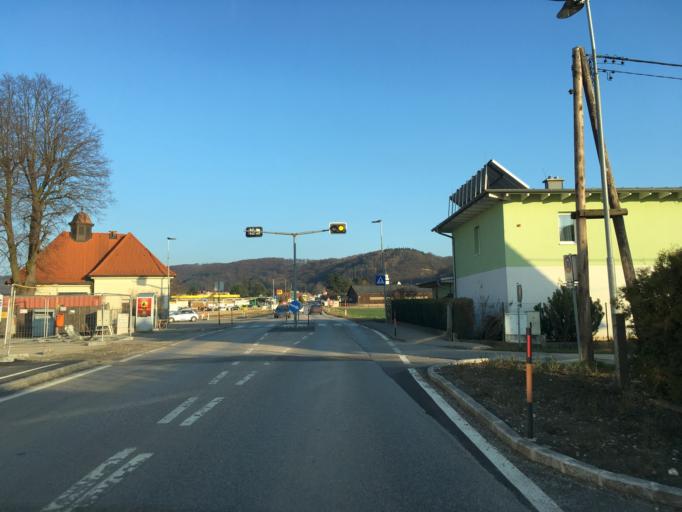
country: AT
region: Lower Austria
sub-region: Politischer Bezirk Tulln
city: Wordern
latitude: 48.3230
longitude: 16.1972
